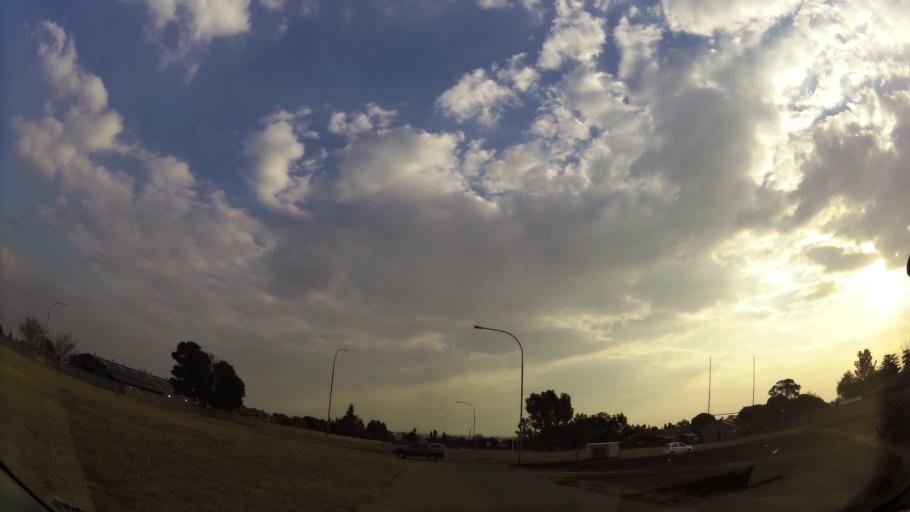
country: ZA
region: Gauteng
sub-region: Ekurhuleni Metropolitan Municipality
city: Benoni
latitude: -26.1597
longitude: 28.3021
